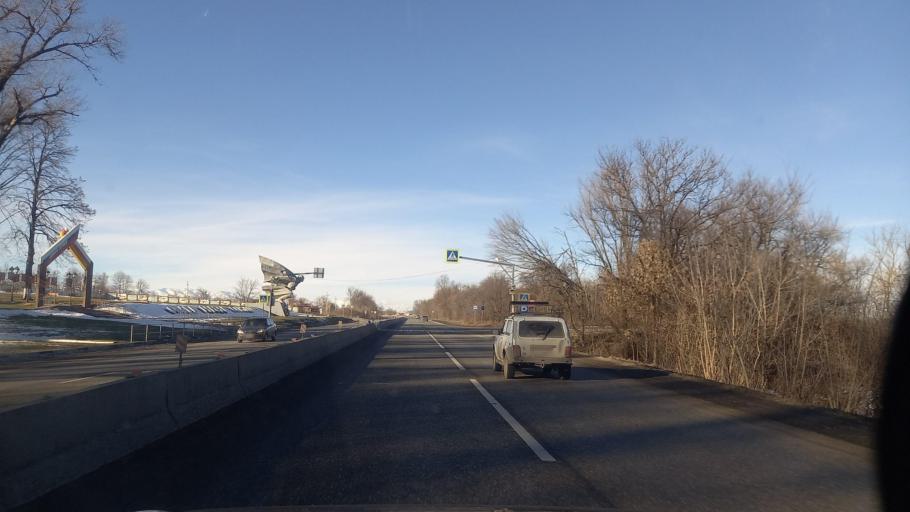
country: RU
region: North Ossetia
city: Gizel'
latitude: 43.0287
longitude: 44.5871
